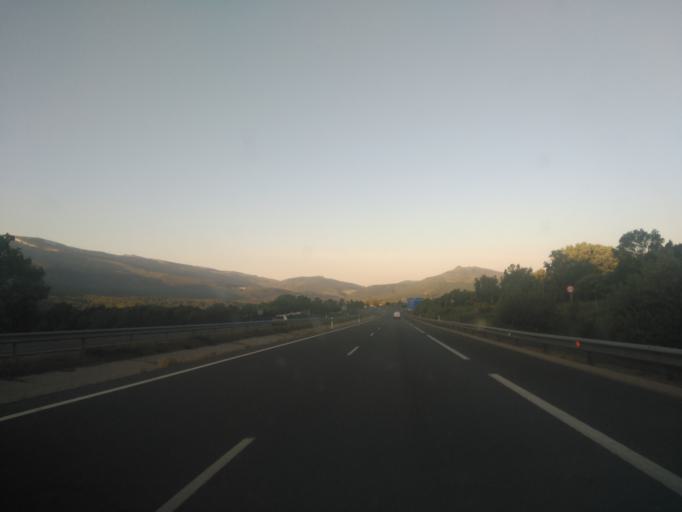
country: ES
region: Castille and Leon
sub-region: Provincia de Salamanca
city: Vallejera de Riofrio
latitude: 40.4173
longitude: -5.7139
